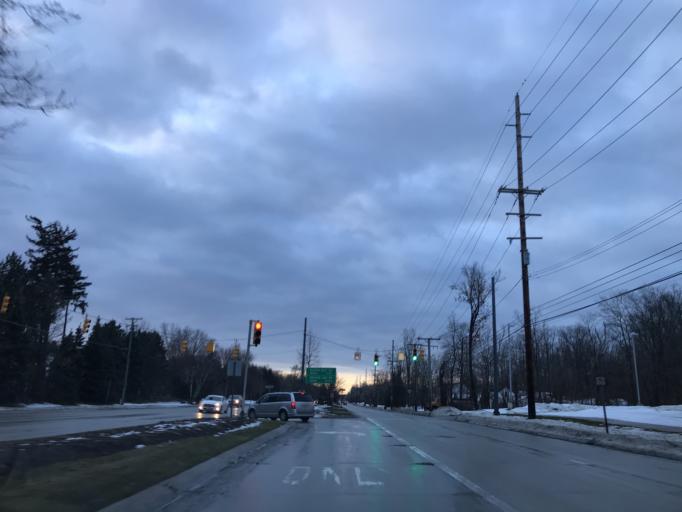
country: US
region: Michigan
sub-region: Oakland County
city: Farmington Hills
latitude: 42.4834
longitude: -83.3580
